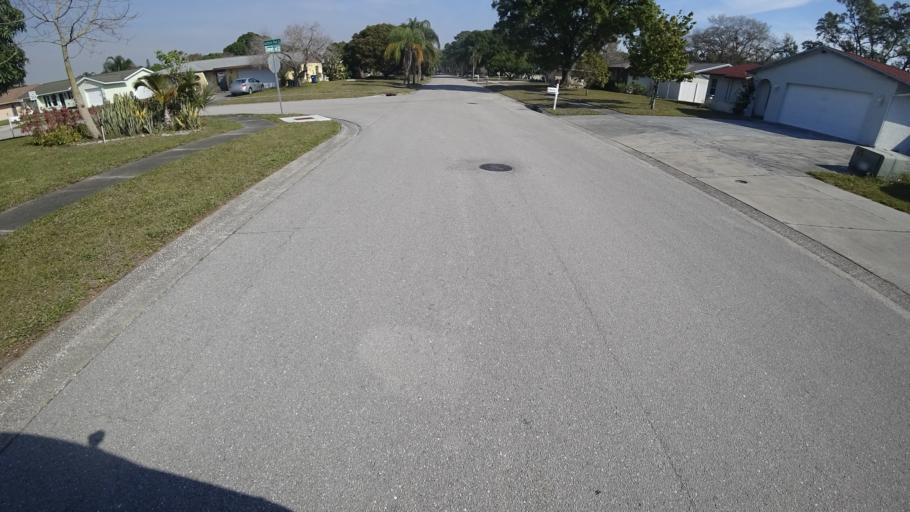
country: US
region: Florida
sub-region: Manatee County
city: Whitfield
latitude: 27.4095
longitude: -82.5514
